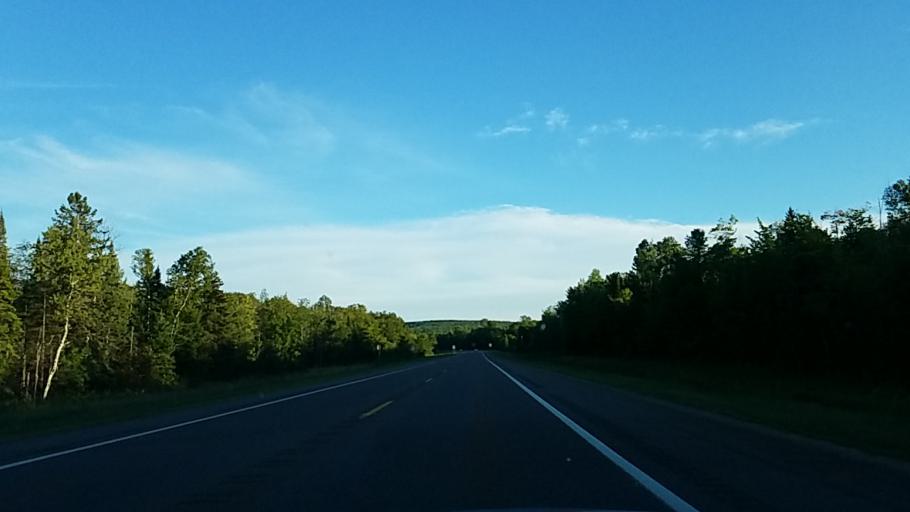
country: US
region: Michigan
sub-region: Alger County
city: Munising
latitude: 46.4477
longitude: -86.8879
